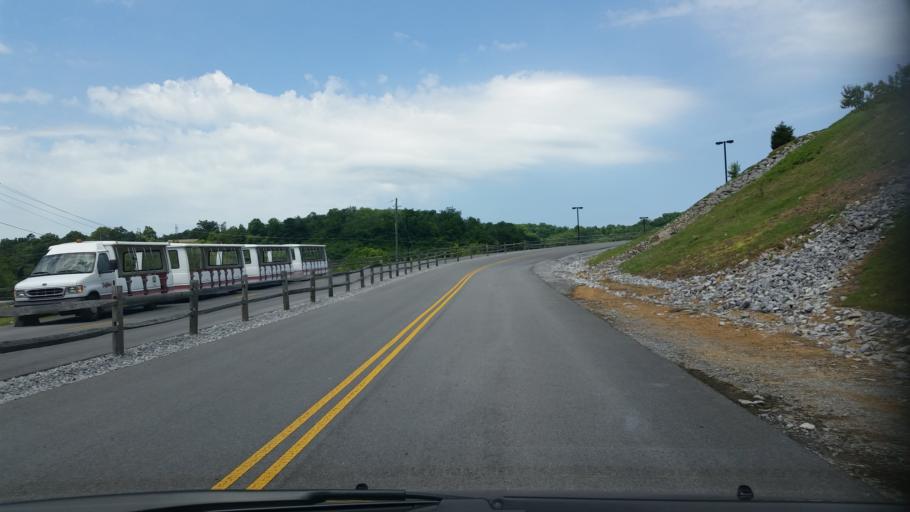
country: US
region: Tennessee
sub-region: Sevier County
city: Pigeon Forge
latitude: 35.8068
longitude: -83.5335
